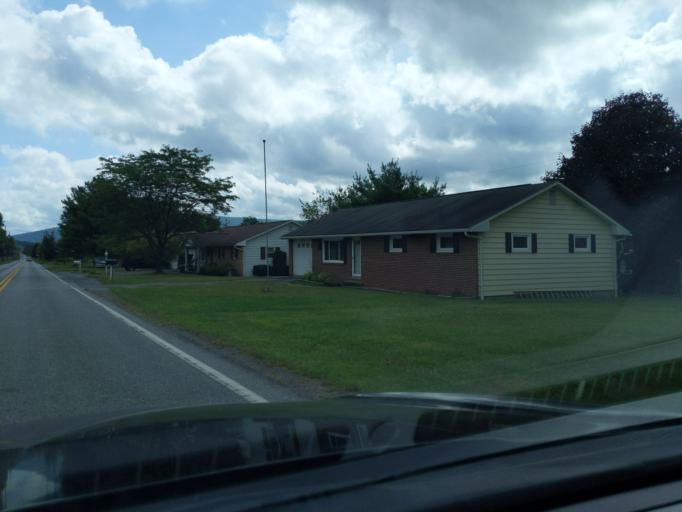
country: US
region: Pennsylvania
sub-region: Blair County
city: Duncansville
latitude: 40.3906
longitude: -78.4526
